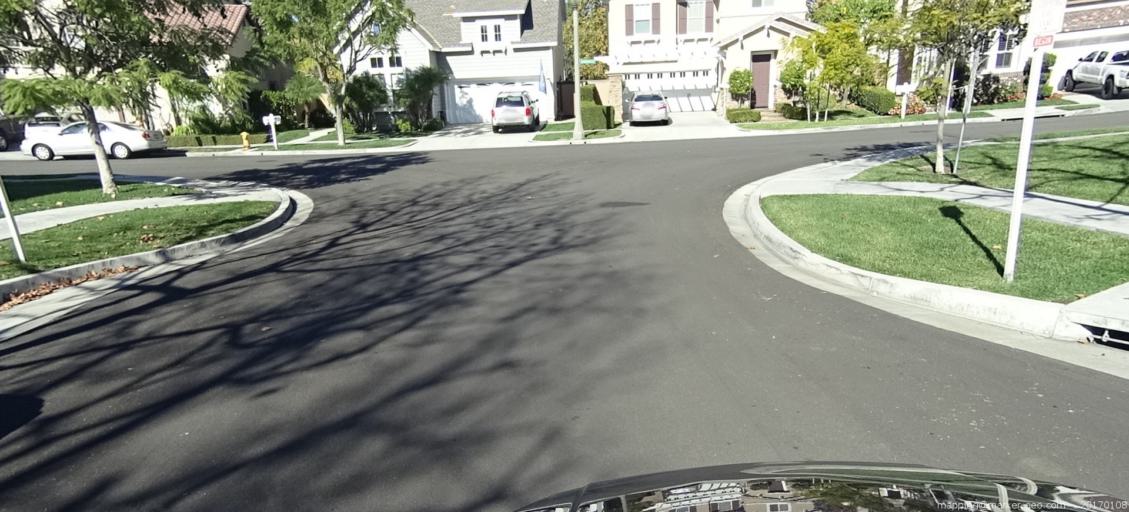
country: US
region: California
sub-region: Orange County
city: Ladera Ranch
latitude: 33.5683
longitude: -117.6424
